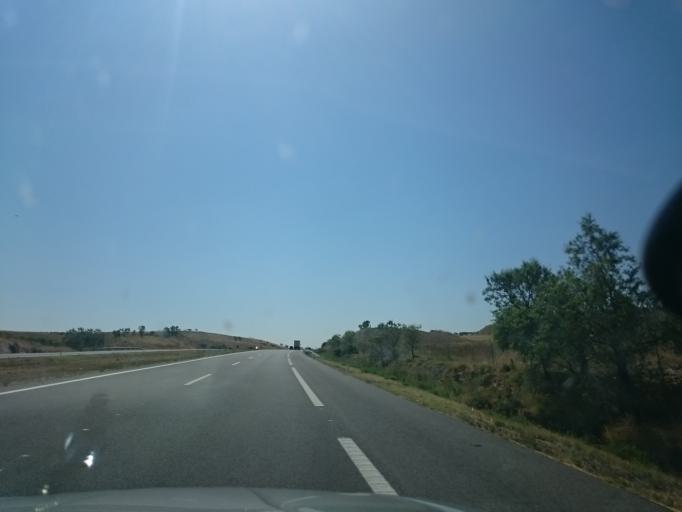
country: ES
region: Navarre
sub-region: Provincia de Navarra
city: Ribaforada
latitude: 41.9771
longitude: -1.5527
